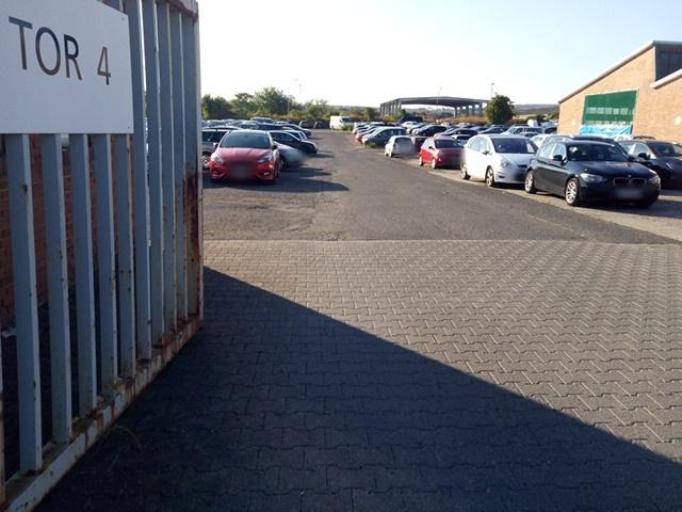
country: DE
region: Rheinland-Pfalz
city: Bad Kreuznach
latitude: 49.8491
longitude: 7.8750
